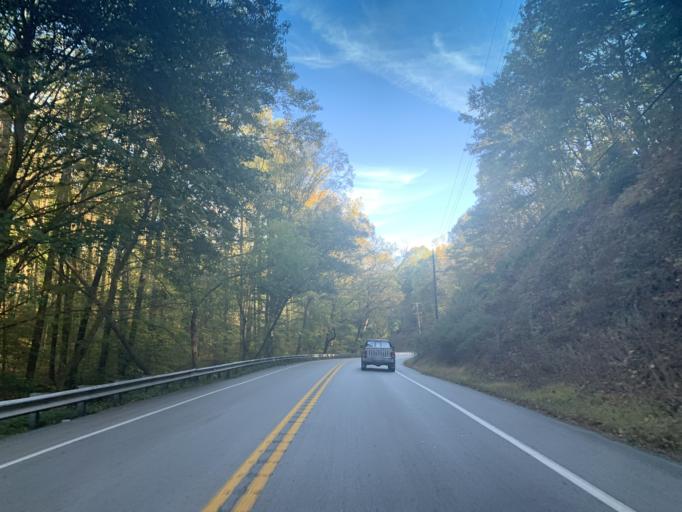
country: US
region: Pennsylvania
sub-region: Chester County
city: Parkesburg
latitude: 39.9493
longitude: -75.9131
